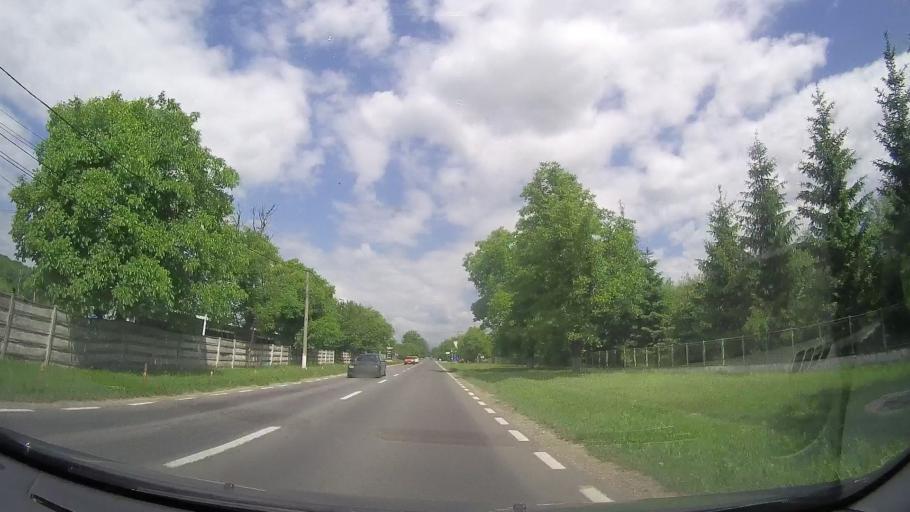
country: RO
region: Prahova
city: Drajna de Jos
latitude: 45.2124
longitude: 26.0388
